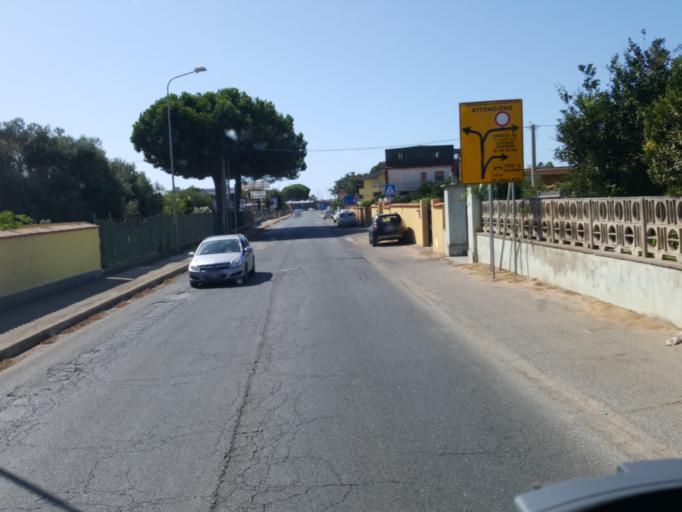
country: IT
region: Latium
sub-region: Citta metropolitana di Roma Capitale
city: Anzio
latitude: 41.5132
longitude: 12.6339
